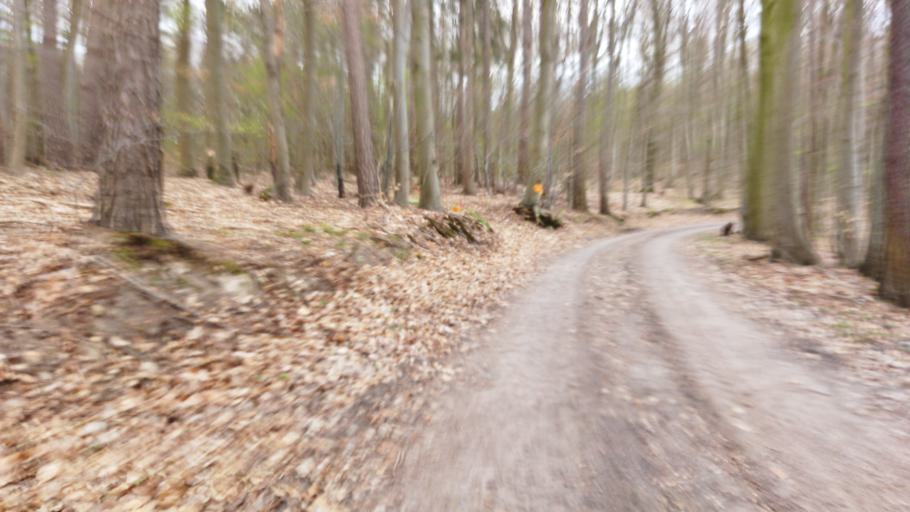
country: DE
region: Baden-Wuerttemberg
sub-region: Regierungsbezirk Stuttgart
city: Eberstadt
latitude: 49.2031
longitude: 9.2993
